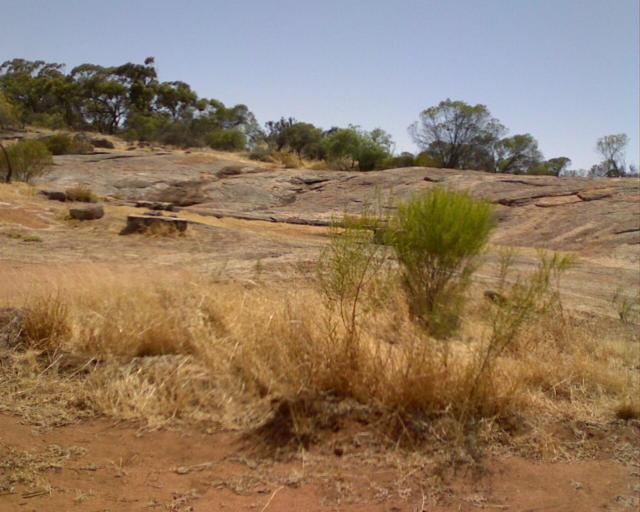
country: AU
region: Western Australia
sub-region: Wongan-Ballidu
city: Wongan Hills
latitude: -30.4233
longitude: 116.9678
